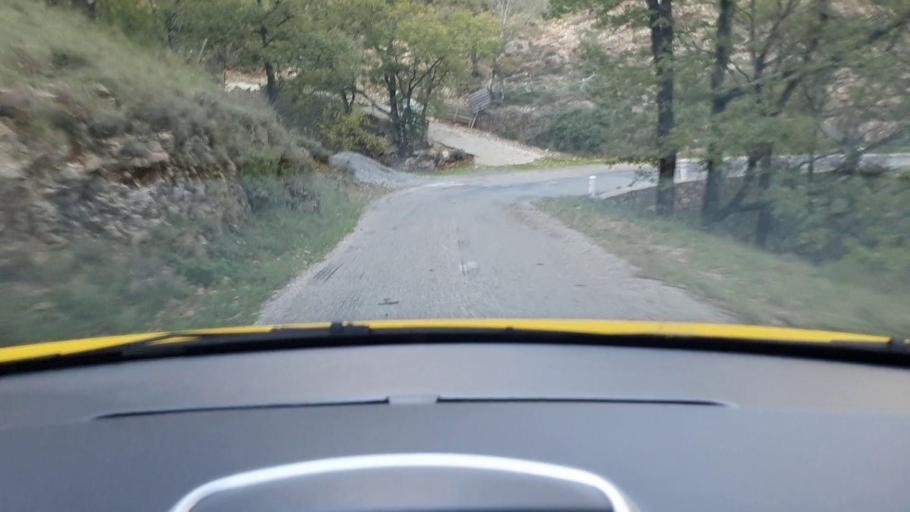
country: FR
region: Languedoc-Roussillon
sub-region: Departement du Gard
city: Sumene
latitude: 43.9795
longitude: 3.7626
